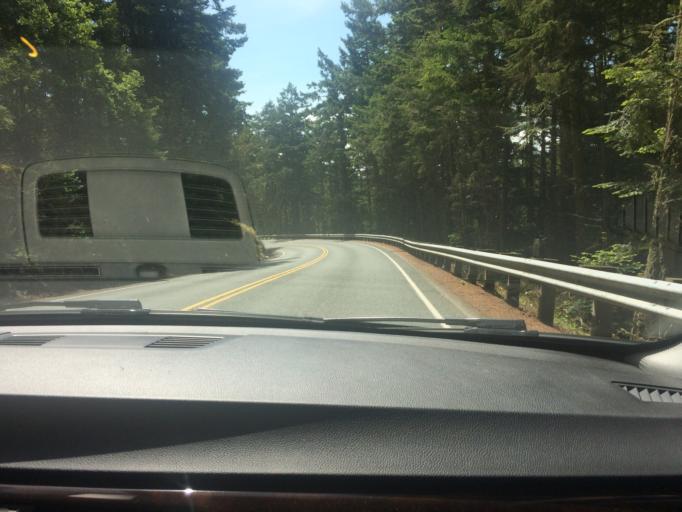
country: US
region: Washington
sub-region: Island County
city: Ault Field
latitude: 48.4191
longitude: -122.6491
